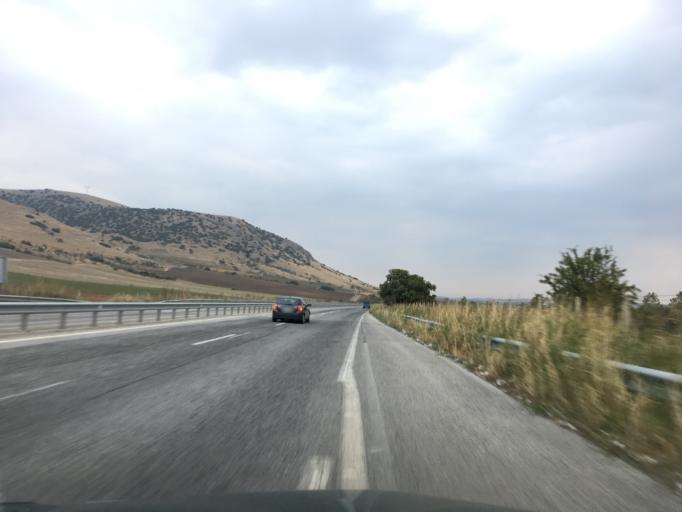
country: GR
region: Thessaly
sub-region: Trikala
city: Zarkos
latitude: 39.5955
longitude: 22.1829
